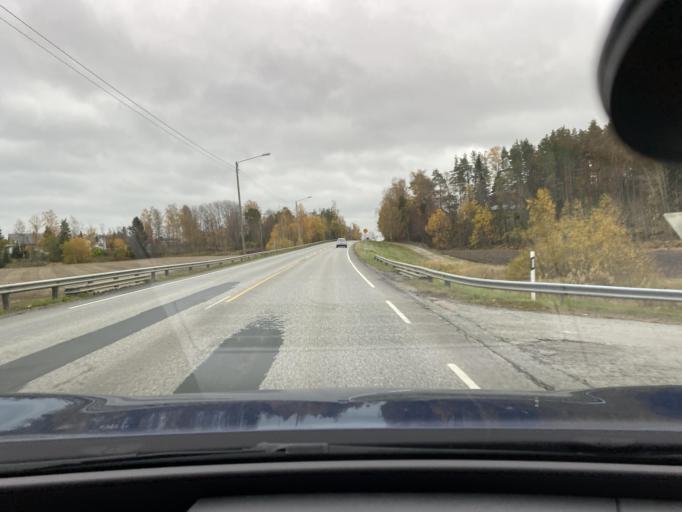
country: FI
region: Varsinais-Suomi
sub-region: Vakka-Suomi
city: Pyhaeranta
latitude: 60.9880
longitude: 21.5851
